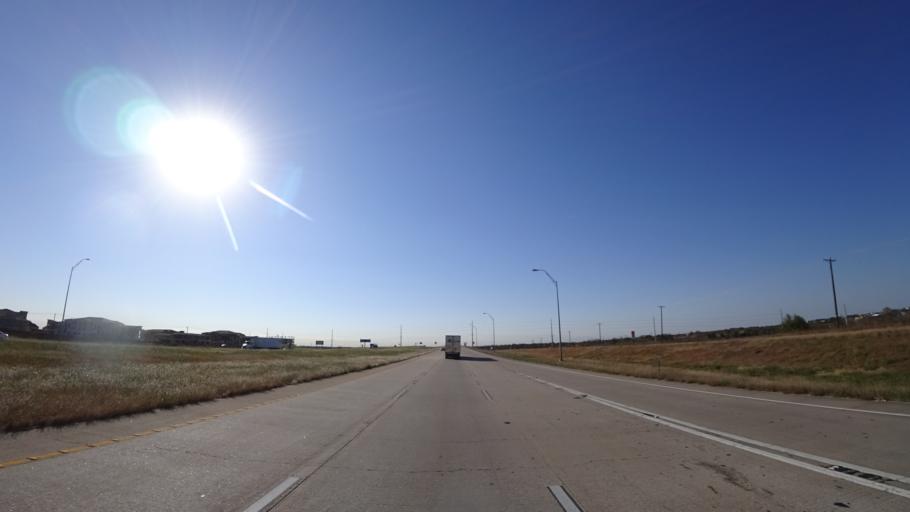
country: US
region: Texas
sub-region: Travis County
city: Pflugerville
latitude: 30.4569
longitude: -97.5946
